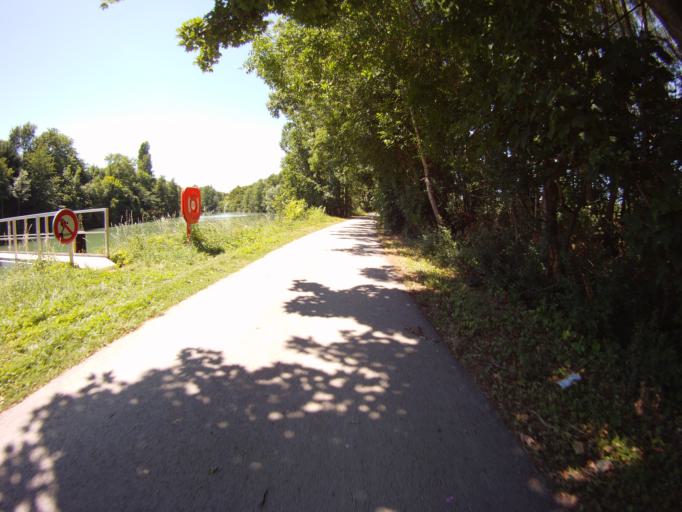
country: FR
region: Champagne-Ardenne
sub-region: Departement de la Marne
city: Damery
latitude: 49.0666
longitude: 3.9036
